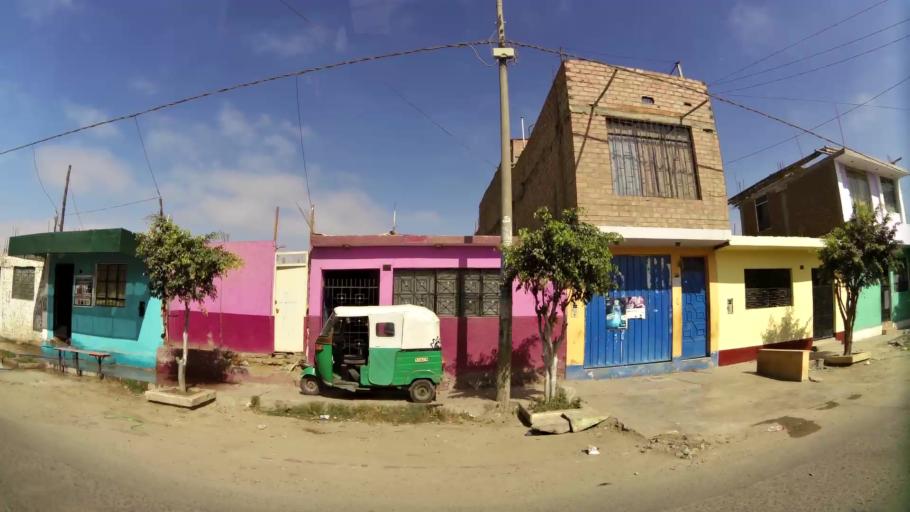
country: PE
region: Ica
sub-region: Provincia de Ica
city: Ica
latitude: -14.0671
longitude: -75.7219
